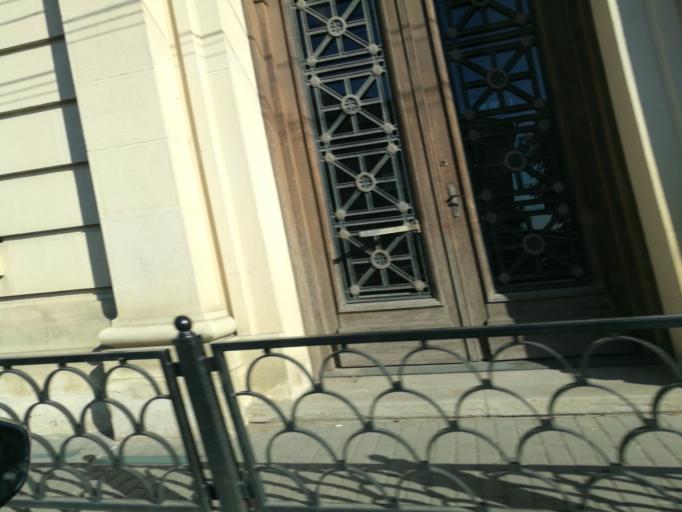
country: RO
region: Iasi
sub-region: Municipiul Iasi
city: Iasi
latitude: 47.1700
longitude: 27.5753
